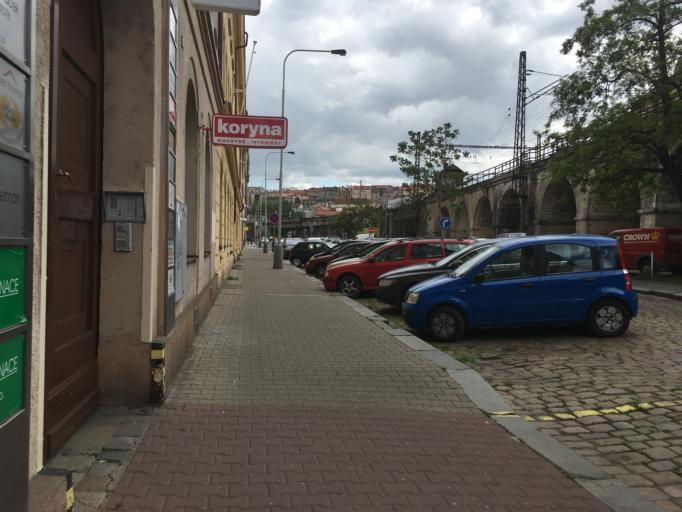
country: CZ
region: Praha
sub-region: Praha 8
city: Karlin
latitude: 50.0916
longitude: 14.4425
